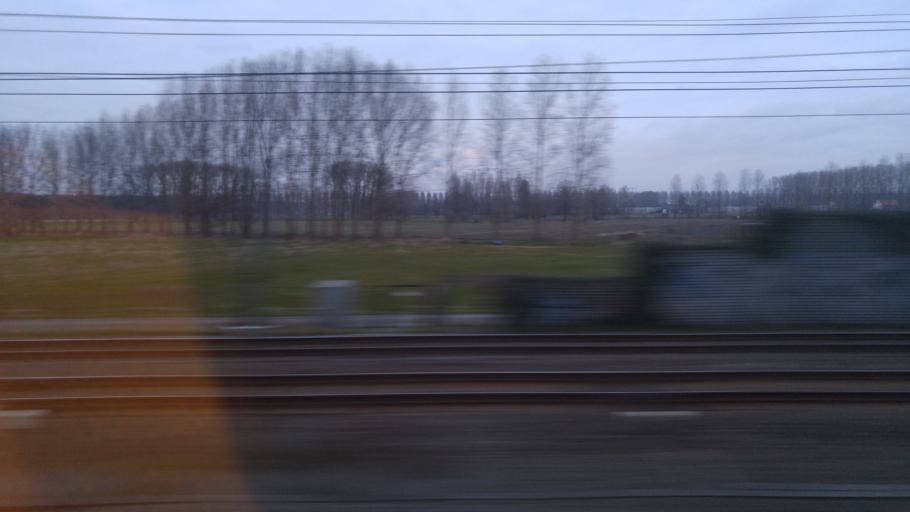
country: NL
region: North Brabant
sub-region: Gemeente Best
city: Best
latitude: 51.5238
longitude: 5.3761
